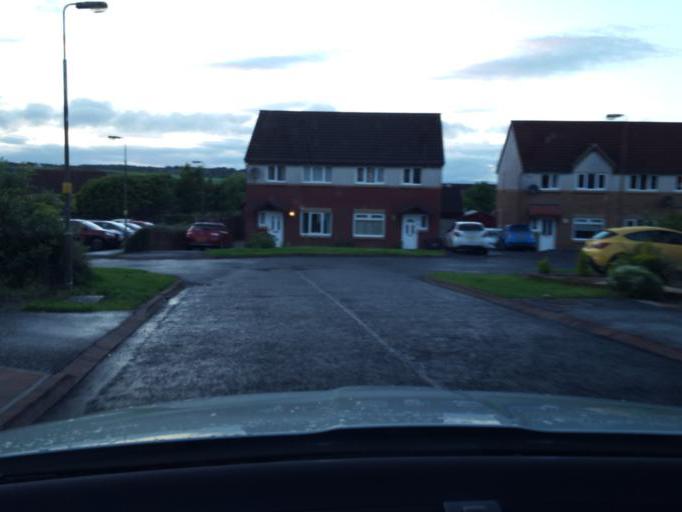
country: GB
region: Scotland
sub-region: West Lothian
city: Armadale
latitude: 55.8976
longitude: -3.7137
